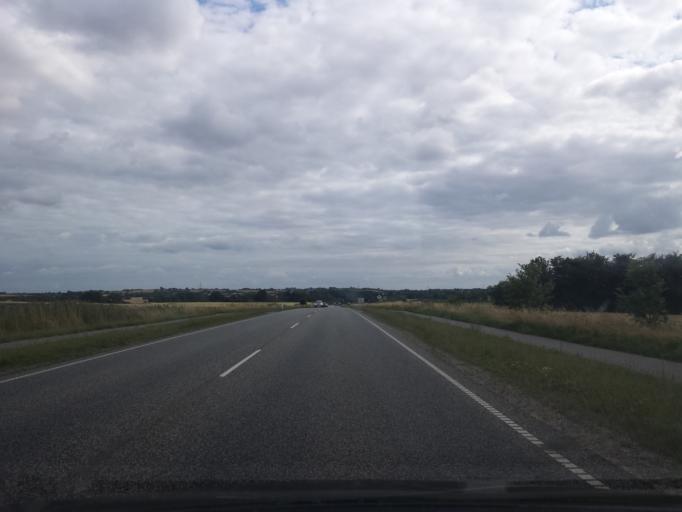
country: DK
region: South Denmark
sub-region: Sonderborg Kommune
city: Augustenborg
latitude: 54.9594
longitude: 9.8996
